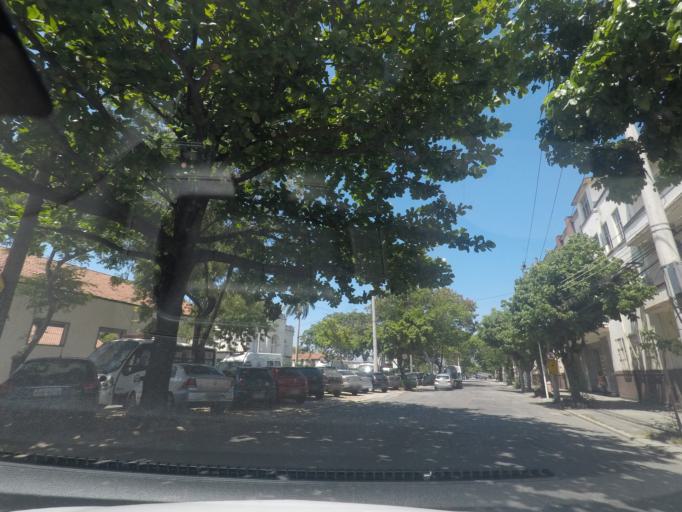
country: BR
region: Rio de Janeiro
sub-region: Rio De Janeiro
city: Rio de Janeiro
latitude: -22.9031
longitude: -43.2135
